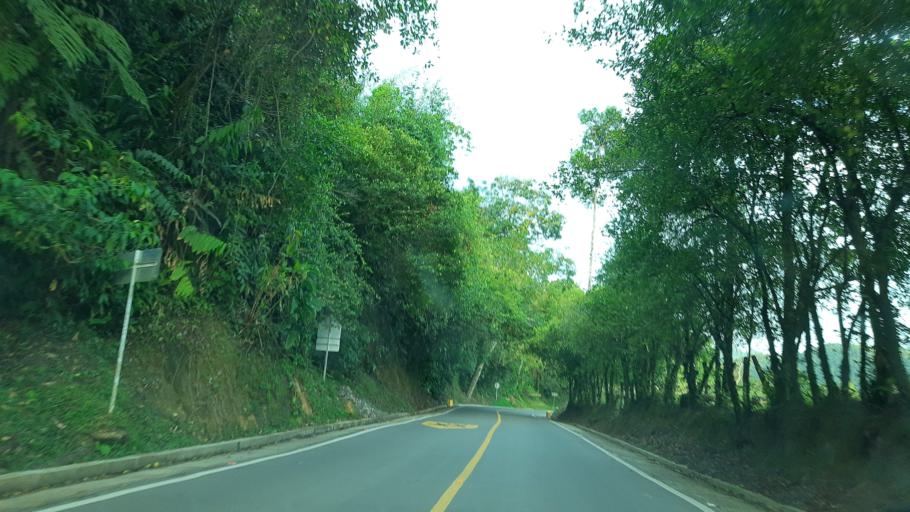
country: CO
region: Boyaca
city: San Luis de Gaceno
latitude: 4.8164
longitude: -73.1805
